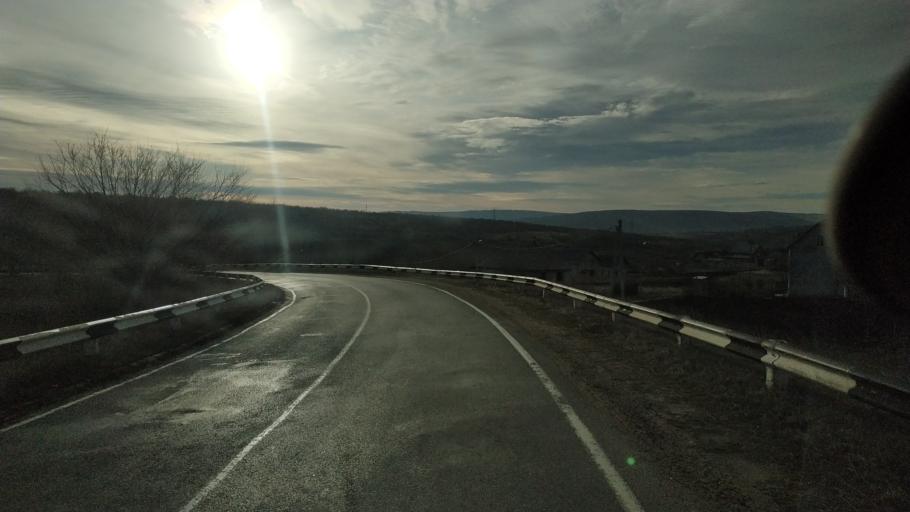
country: MD
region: Chisinau
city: Vadul lui Voda
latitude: 47.0698
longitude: 29.0182
